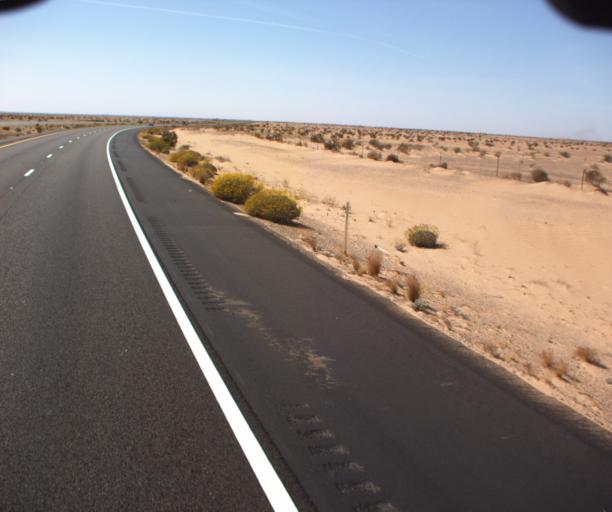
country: US
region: Arizona
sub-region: Yuma County
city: Somerton
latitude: 32.4960
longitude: -114.5664
